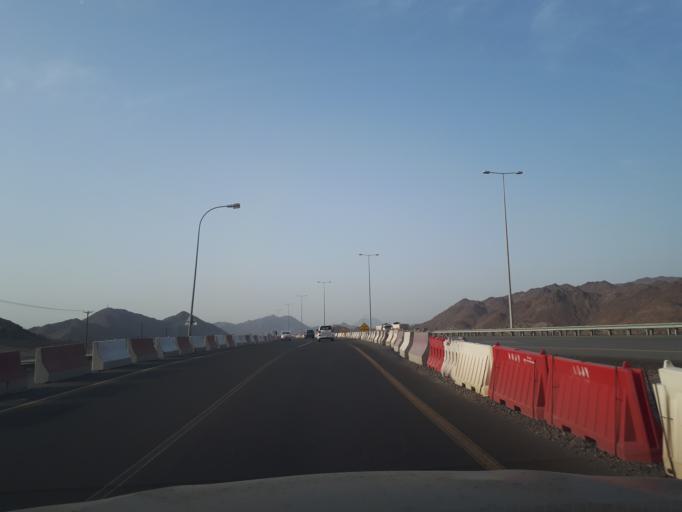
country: OM
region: Muhafazat ad Dakhiliyah
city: Sufalat Sama'il
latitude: 23.2909
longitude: 58.1093
